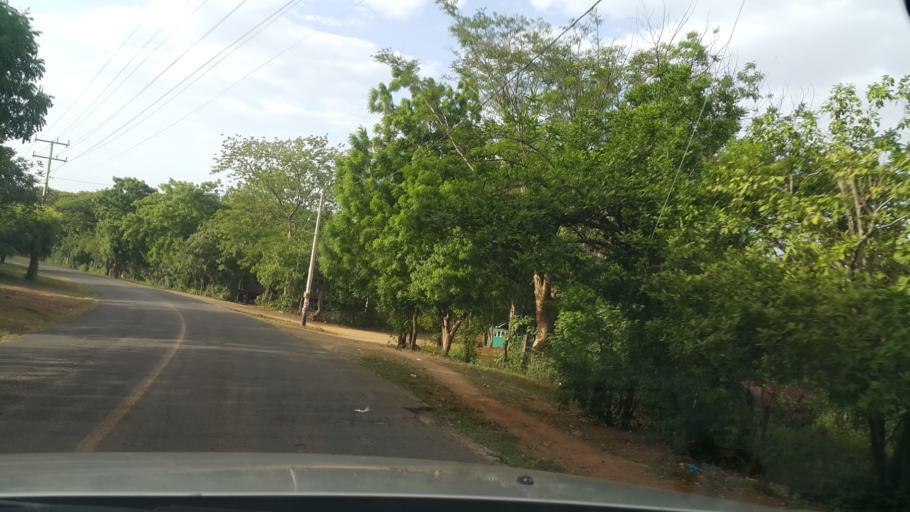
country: NI
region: Managua
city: San Rafael del Sur
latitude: 11.8194
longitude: -86.4750
